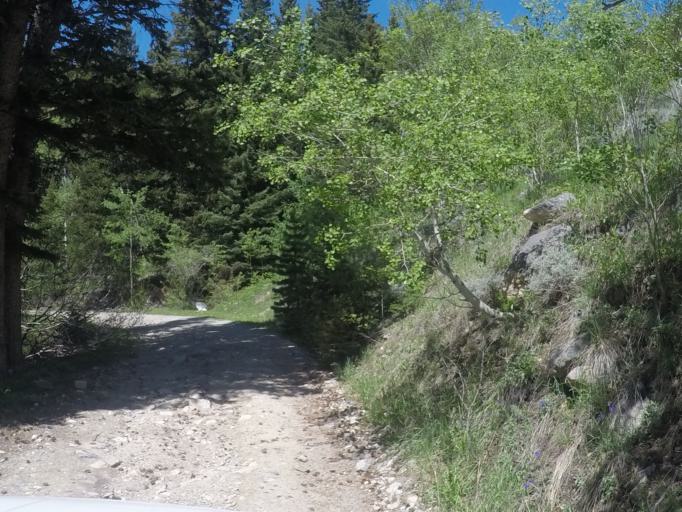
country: US
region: Montana
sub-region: Carbon County
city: Red Lodge
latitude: 45.0574
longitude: -109.4233
